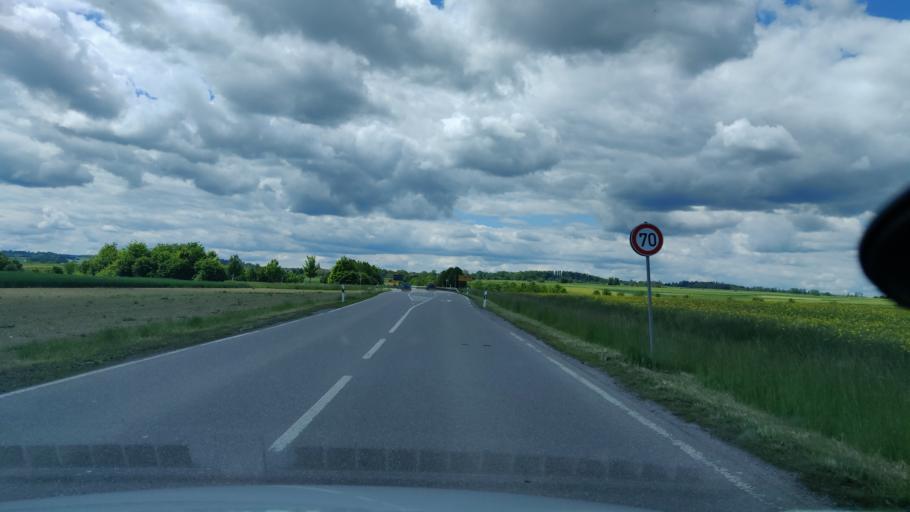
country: DE
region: Baden-Wuerttemberg
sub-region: Regierungsbezirk Stuttgart
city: Motzingen
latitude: 48.4998
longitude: 8.7959
